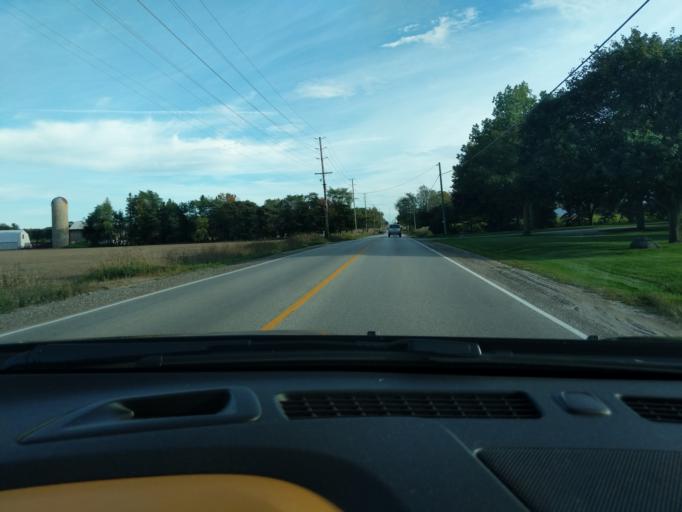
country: CA
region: Ontario
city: Barrie
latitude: 44.4057
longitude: -79.7458
